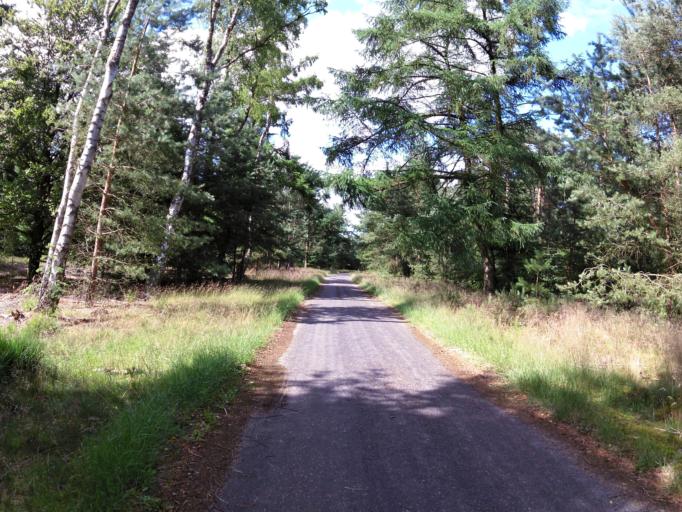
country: NL
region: North Brabant
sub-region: Gemeente Valkenswaard
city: Valkenswaard
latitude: 51.3186
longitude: 5.5108
